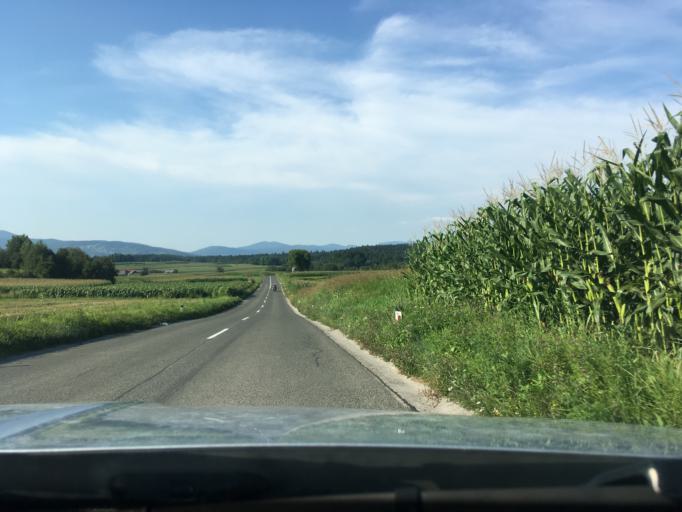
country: SI
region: Crnomelj
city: Crnomelj
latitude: 45.5316
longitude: 15.1630
